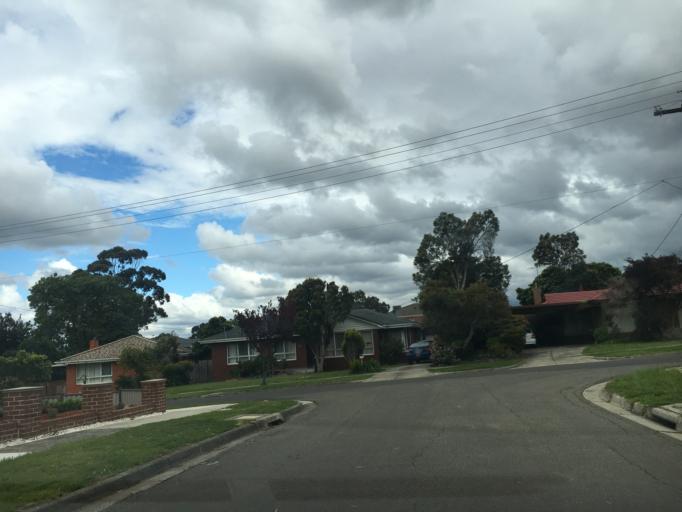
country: AU
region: Victoria
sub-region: Whitehorse
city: Vermont South
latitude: -37.8733
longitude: 145.1737
